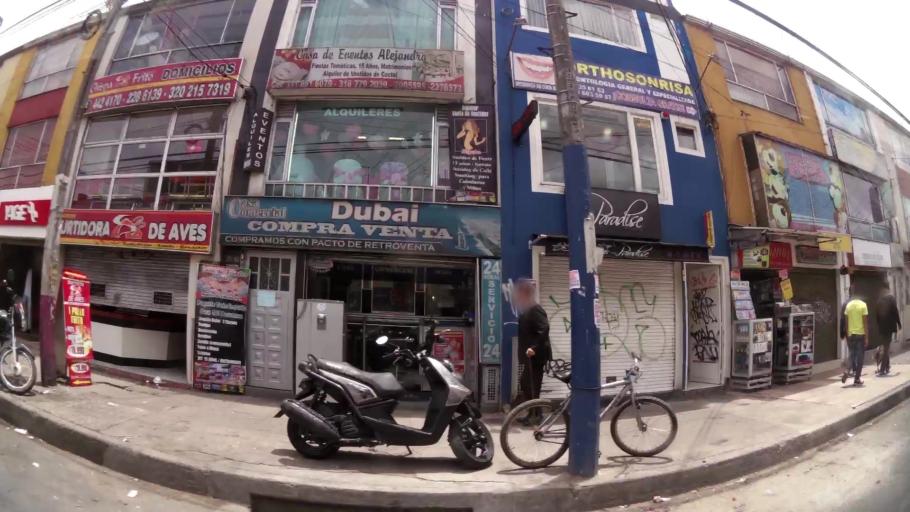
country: CO
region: Cundinamarca
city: Funza
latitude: 4.7178
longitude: -74.1218
